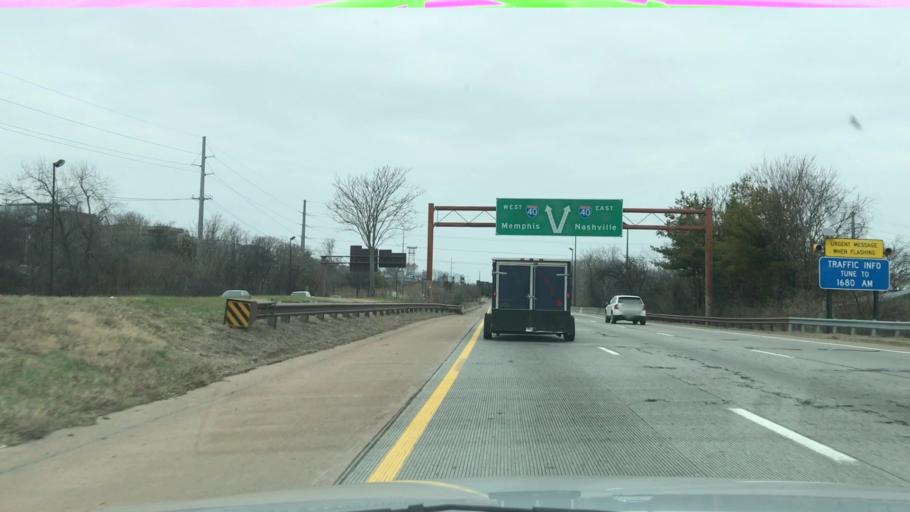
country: US
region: Tennessee
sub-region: Davidson County
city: Nashville
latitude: 36.1469
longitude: -86.8221
